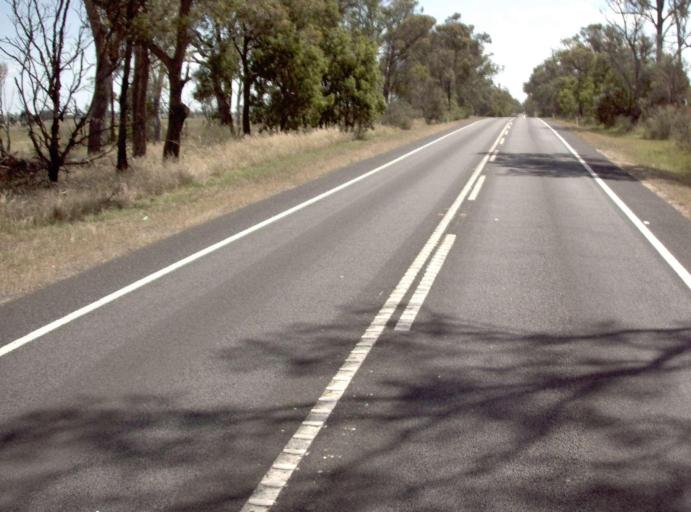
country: AU
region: Victoria
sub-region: Wellington
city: Sale
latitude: -37.9343
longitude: 147.1748
